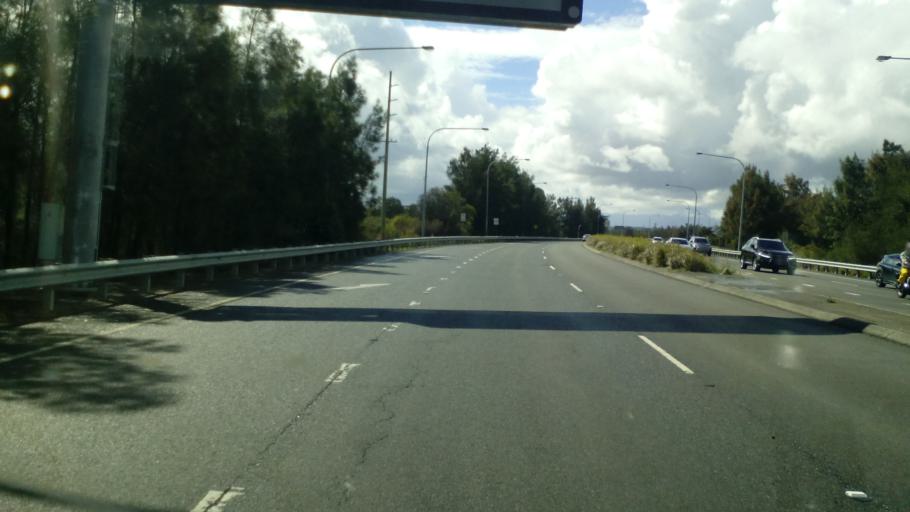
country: AU
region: New South Wales
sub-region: Lake Macquarie Shire
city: Fennell Bay
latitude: -32.9649
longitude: 151.6082
